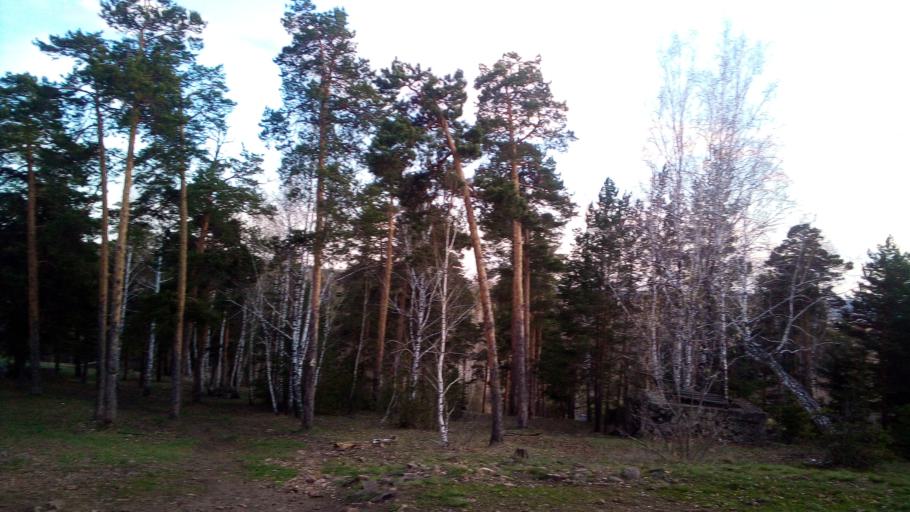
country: RU
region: Chelyabinsk
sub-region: Gorod Chelyabinsk
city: Chelyabinsk
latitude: 55.1598
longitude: 61.3230
